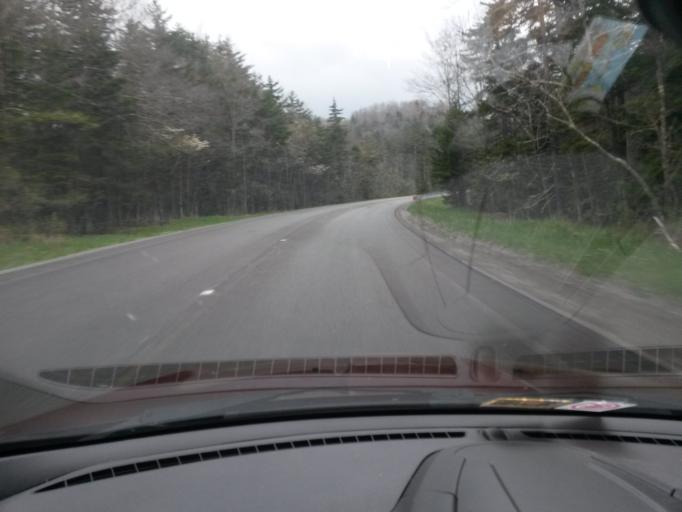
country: US
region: West Virginia
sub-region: Randolph County
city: Elkins
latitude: 38.6235
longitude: -79.8970
